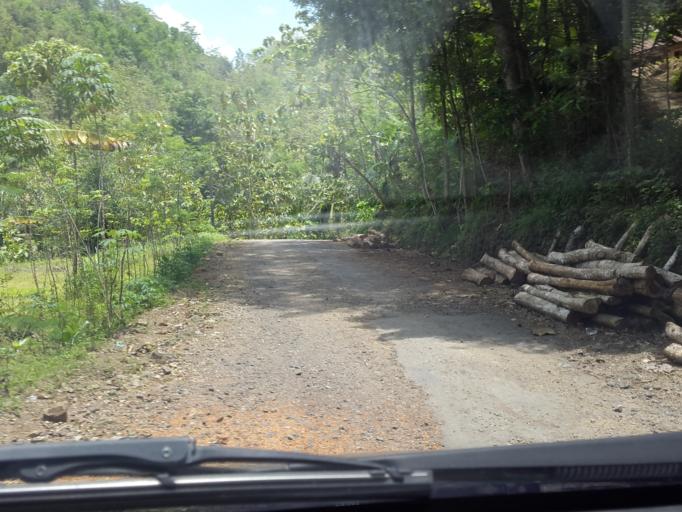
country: ID
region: Daerah Istimewa Yogyakarta
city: Wonosari
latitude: -7.9025
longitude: 110.7492
